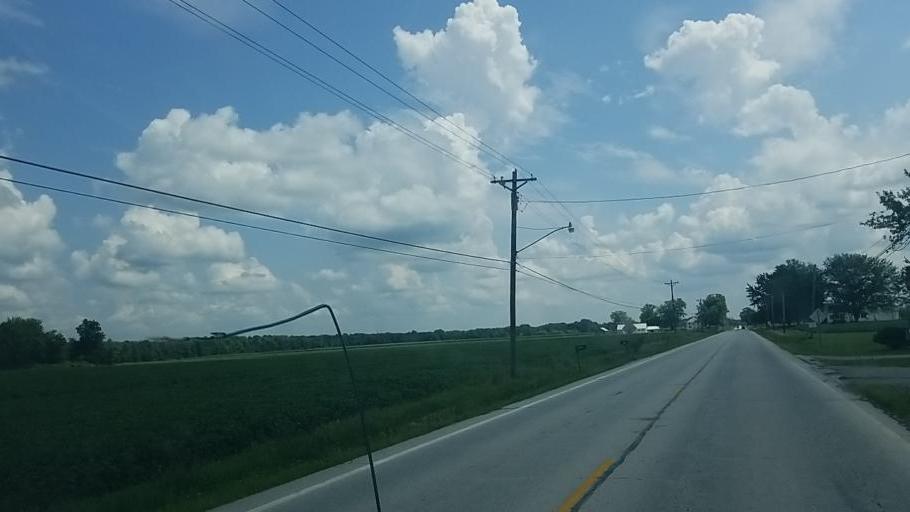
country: US
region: Ohio
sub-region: Wayne County
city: West Salem
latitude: 41.0272
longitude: -82.1236
